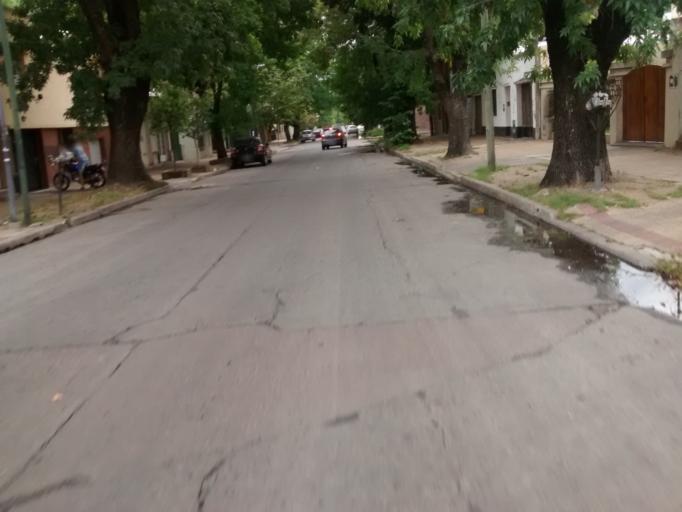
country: AR
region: Buenos Aires
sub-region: Partido de La Plata
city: La Plata
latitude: -34.9300
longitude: -57.9318
